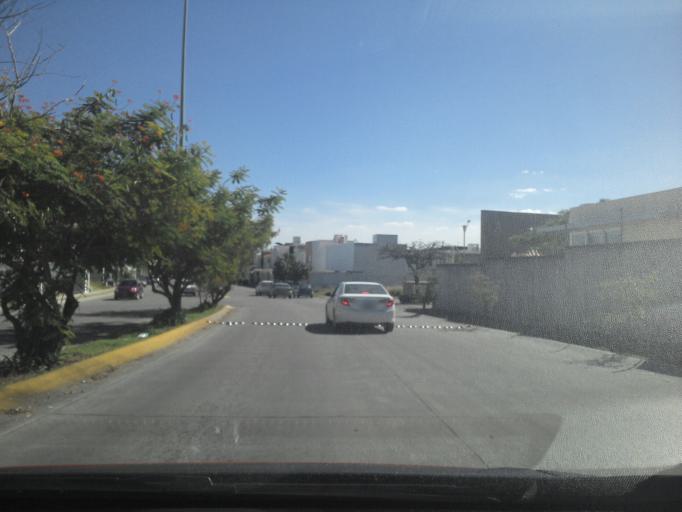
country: MX
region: Jalisco
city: Nuevo Mexico
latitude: 20.7497
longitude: -103.4130
